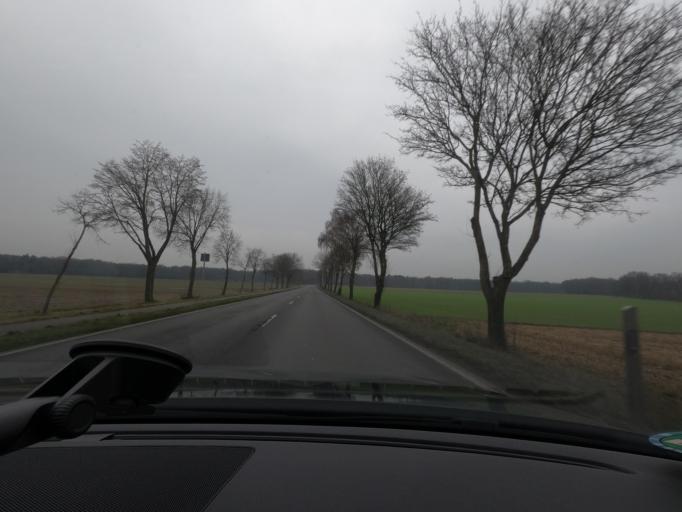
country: DE
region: North Rhine-Westphalia
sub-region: Regierungsbezirk Dusseldorf
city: Nettetal
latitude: 51.3428
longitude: 6.2308
